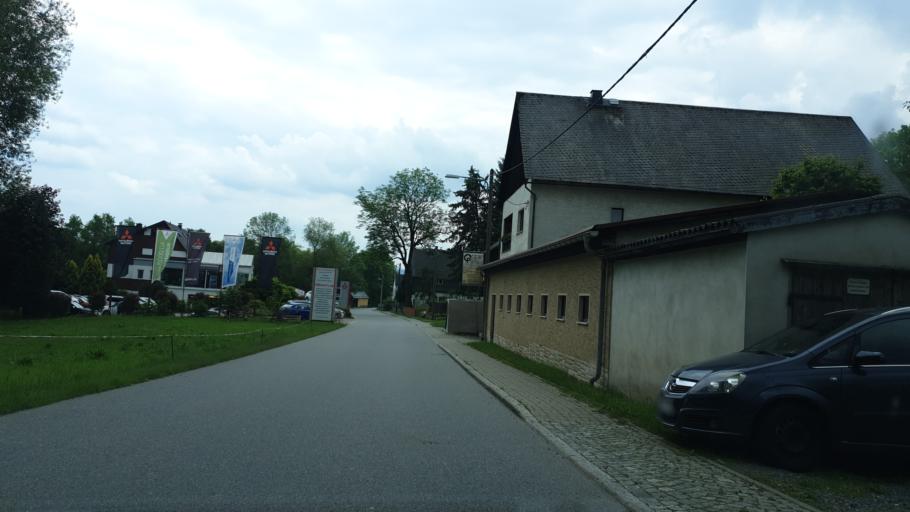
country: DE
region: Saxony
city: Lossnitz
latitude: 50.6265
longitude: 12.7098
